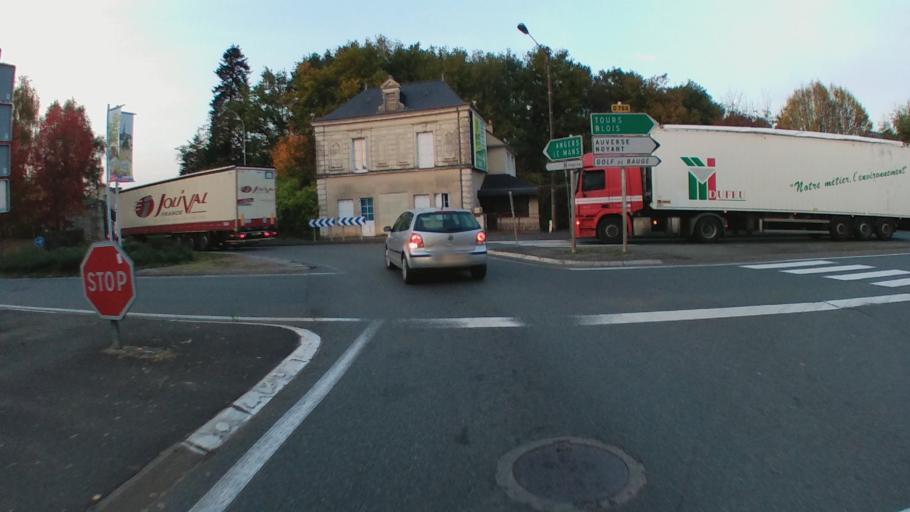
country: FR
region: Pays de la Loire
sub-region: Departement de Maine-et-Loire
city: Bauge-en-Anjou
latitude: 47.5376
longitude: -0.1006
